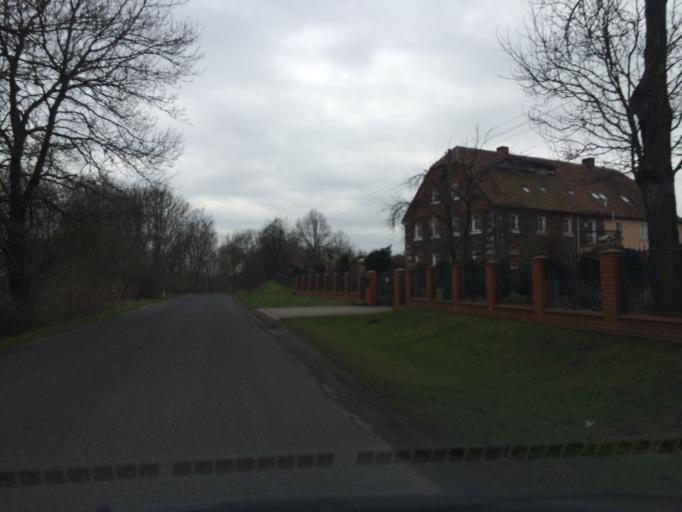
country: PL
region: Lower Silesian Voivodeship
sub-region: Powiat lubanski
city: Luban
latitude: 51.1453
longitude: 15.3137
